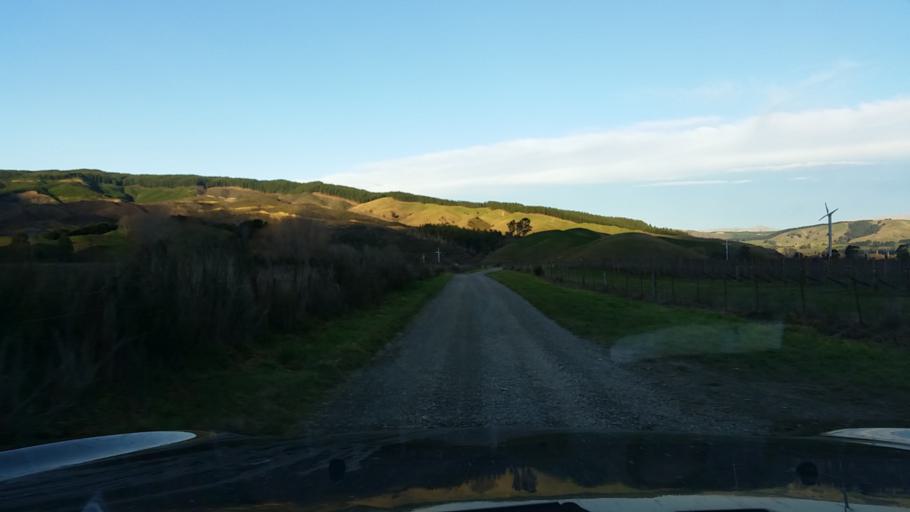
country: NZ
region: Marlborough
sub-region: Marlborough District
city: Blenheim
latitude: -41.5068
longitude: 173.5802
